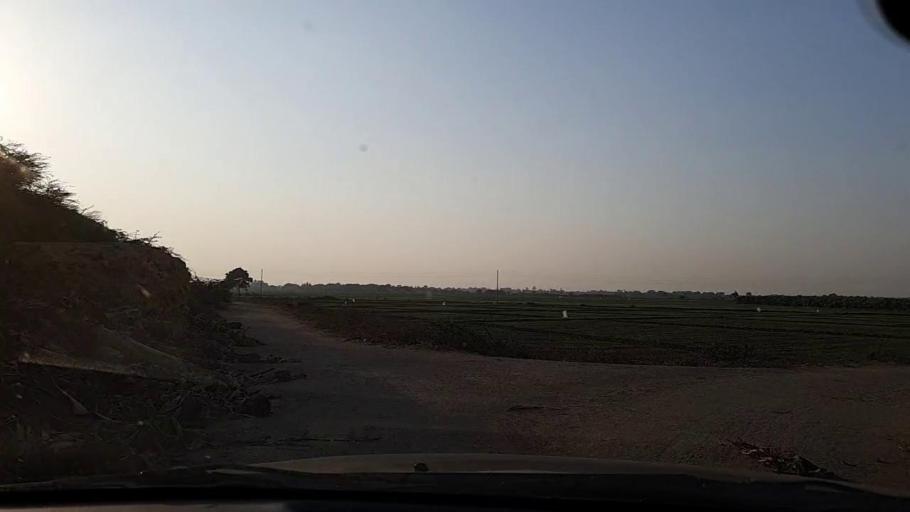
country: PK
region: Sindh
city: Thatta
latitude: 24.5626
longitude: 67.8793
